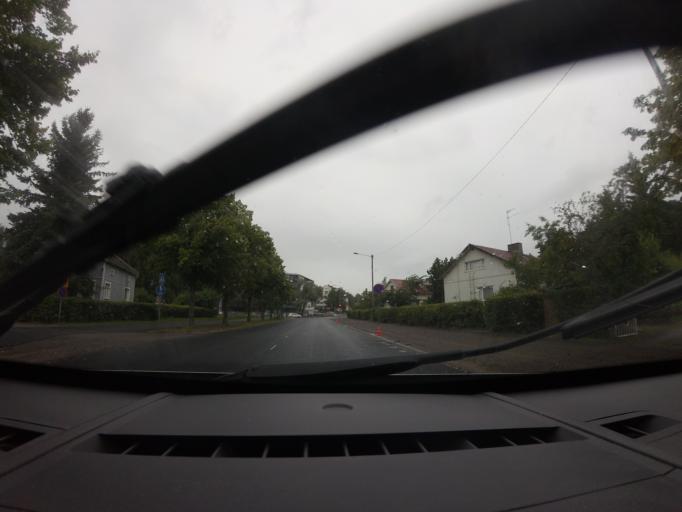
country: FI
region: Varsinais-Suomi
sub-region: Turku
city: Turku
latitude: 60.4347
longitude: 22.2754
